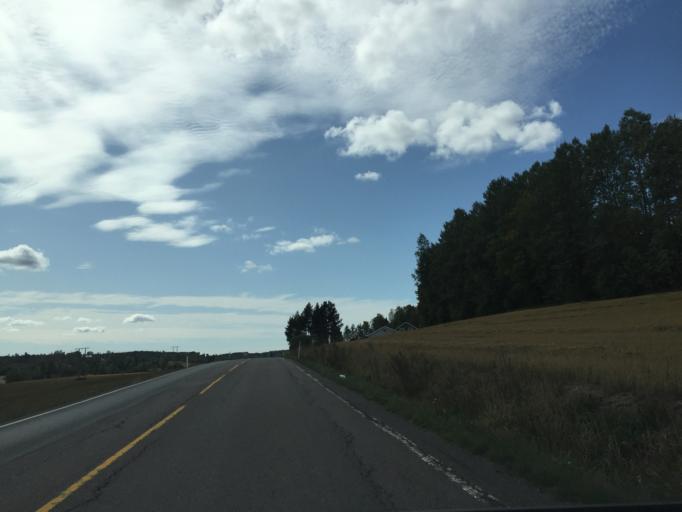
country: NO
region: Ostfold
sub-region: Hobol
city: Elvestad
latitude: 59.6048
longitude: 10.9128
